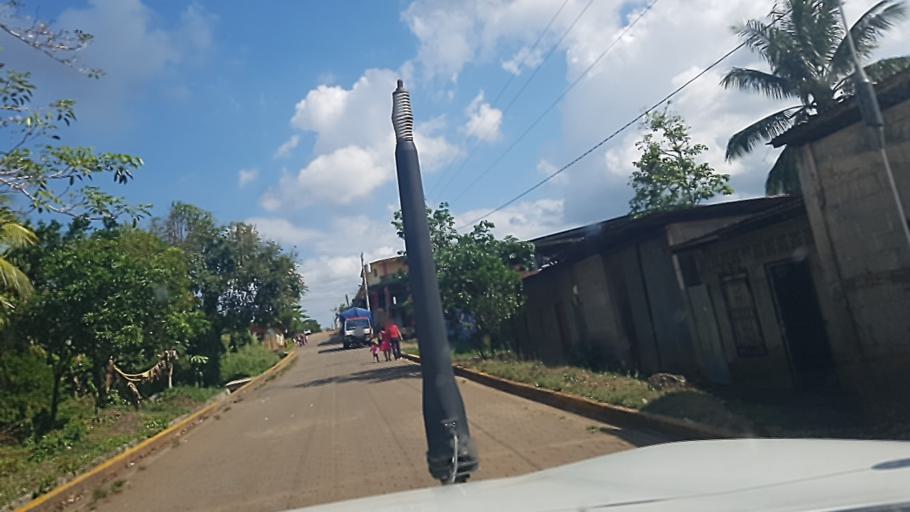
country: NI
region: Atlantico Sur
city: Nueva Guinea
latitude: 11.6884
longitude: -84.4603
